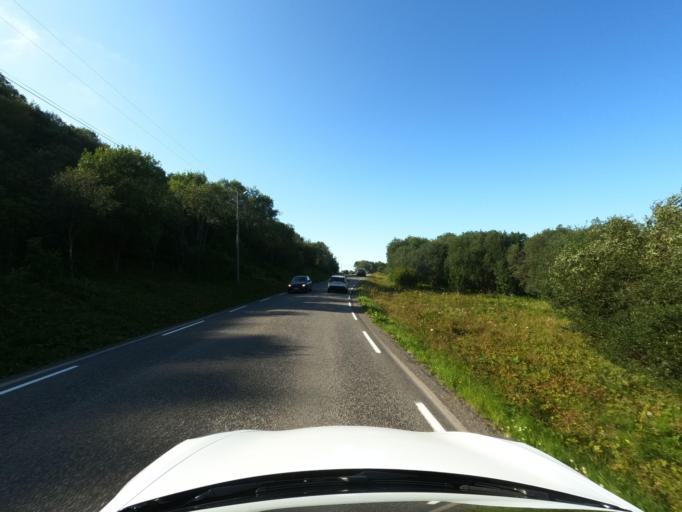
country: NO
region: Nordland
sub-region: Vestvagoy
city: Evjen
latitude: 68.2865
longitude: 13.8870
